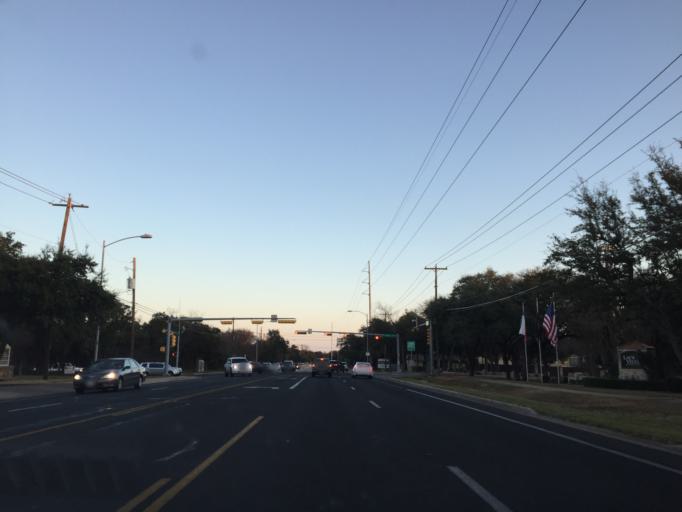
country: US
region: Texas
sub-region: Williamson County
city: Jollyville
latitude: 30.4177
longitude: -97.7507
